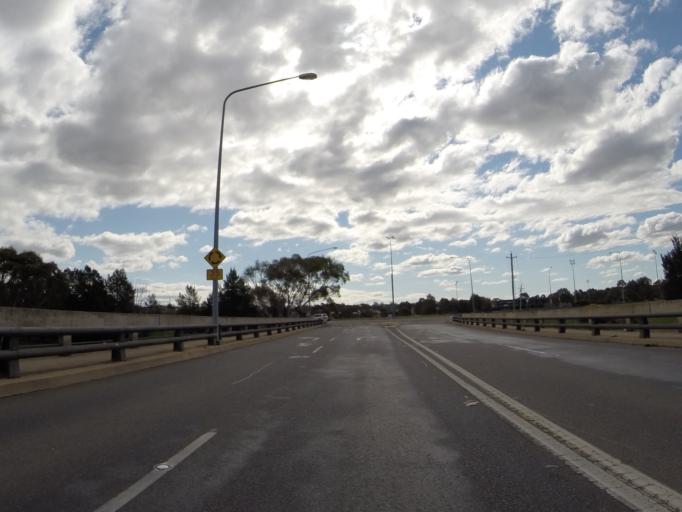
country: AU
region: Australian Capital Territory
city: Belconnen
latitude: -35.2170
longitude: 149.0854
